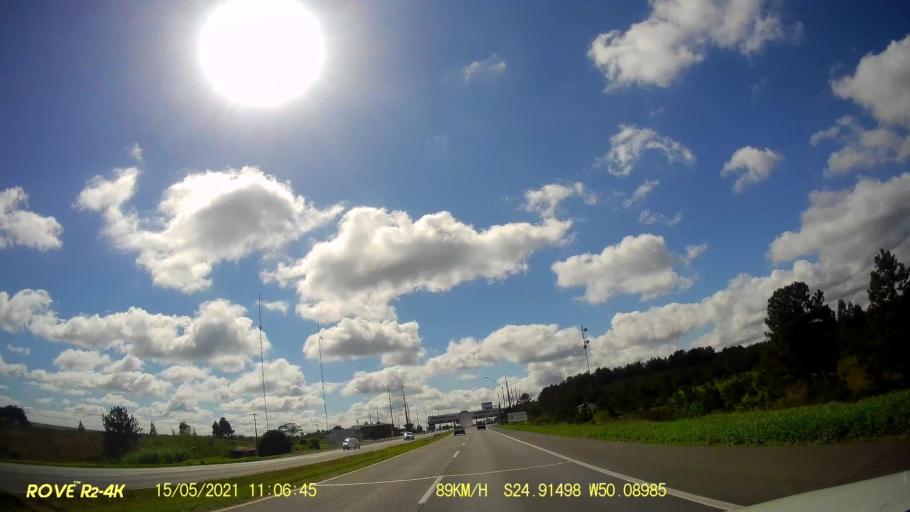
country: BR
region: Parana
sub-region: Carambei
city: Carambei
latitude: -24.9151
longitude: -50.0899
